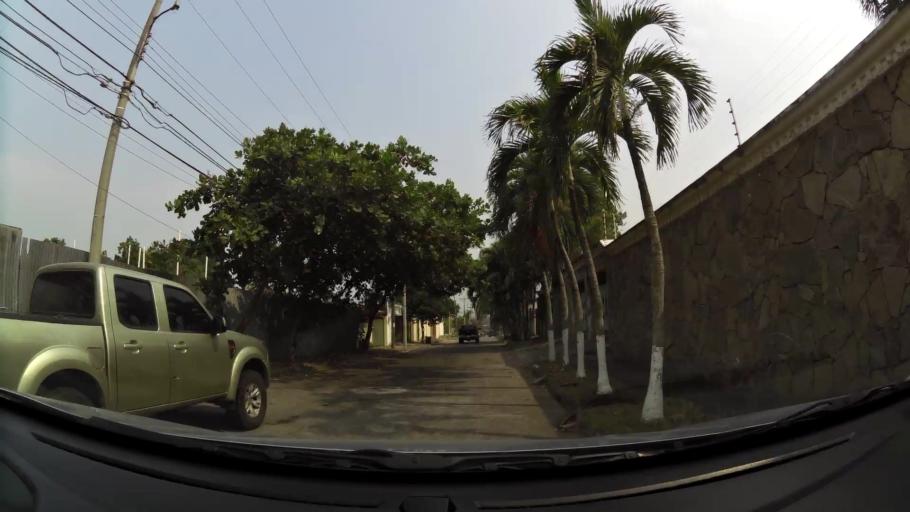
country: HN
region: Cortes
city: Armenta
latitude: 15.4969
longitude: -88.0423
